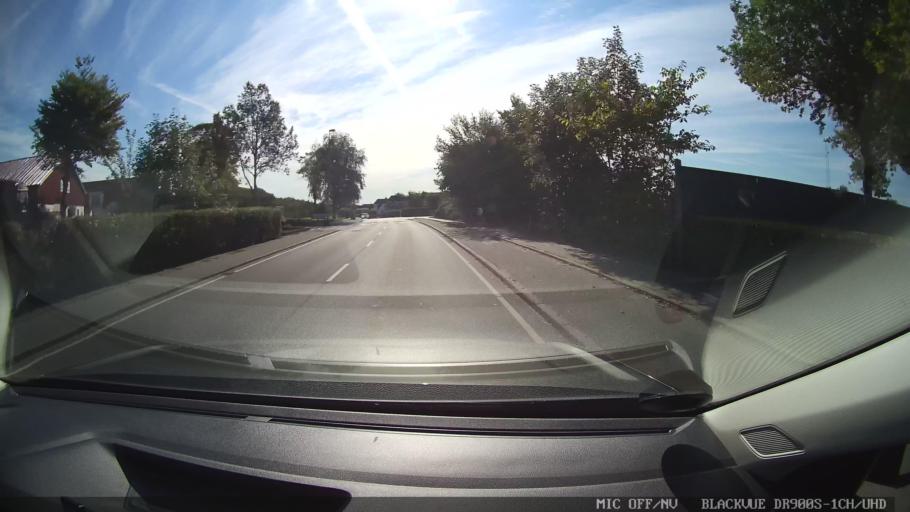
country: DK
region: North Denmark
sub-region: Mariagerfjord Kommune
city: Arden
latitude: 56.7665
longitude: 9.8647
